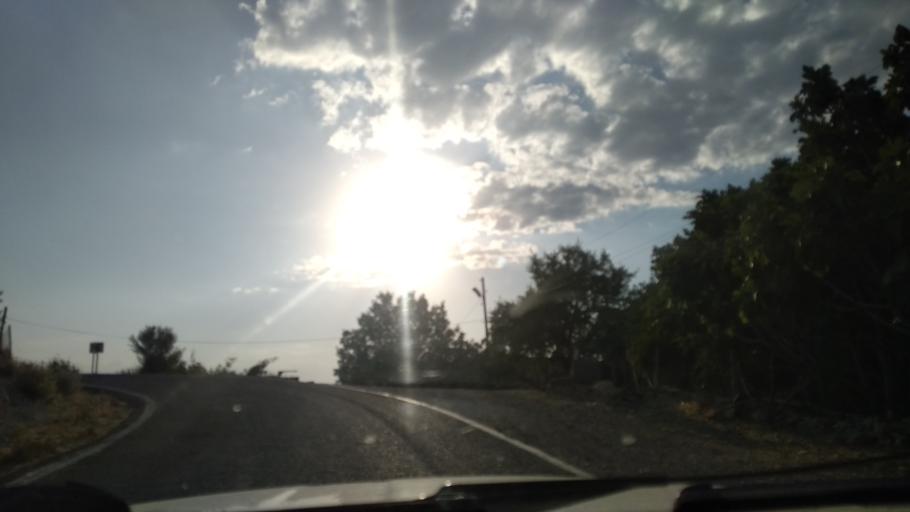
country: TR
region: Mersin
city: Sarikavak
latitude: 36.5760
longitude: 33.6409
